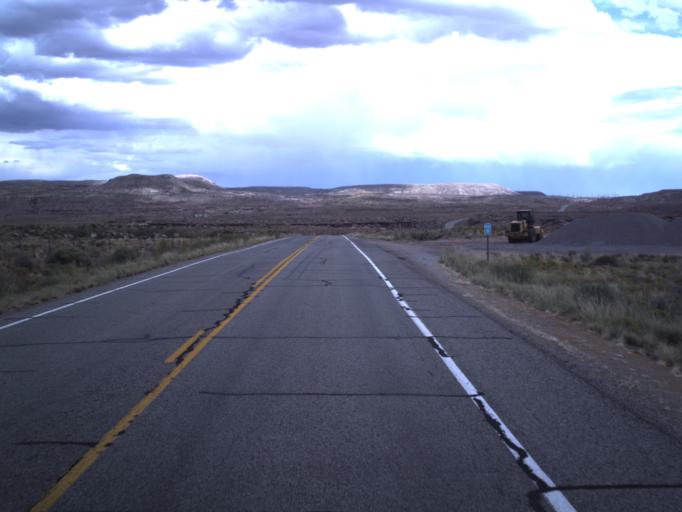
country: US
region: Utah
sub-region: San Juan County
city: Blanding
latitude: 37.2915
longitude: -109.4146
